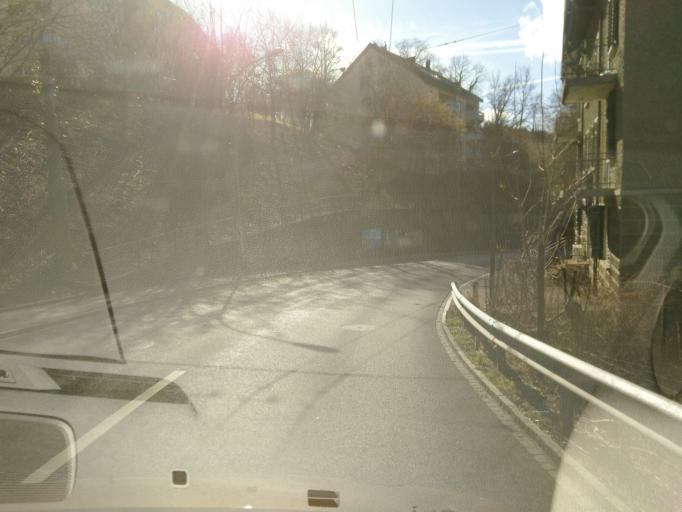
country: CH
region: Appenzell Ausserrhoden
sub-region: Bezirk Hinterland
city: Herisau
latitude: 47.4065
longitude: 9.3248
